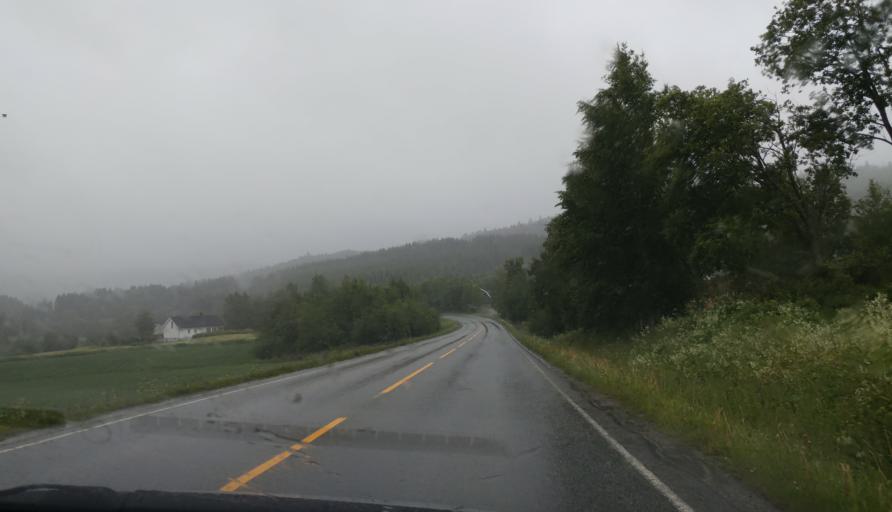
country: NO
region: Nord-Trondelag
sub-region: Stjordal
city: Stjordalshalsen
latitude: 63.4044
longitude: 10.9427
